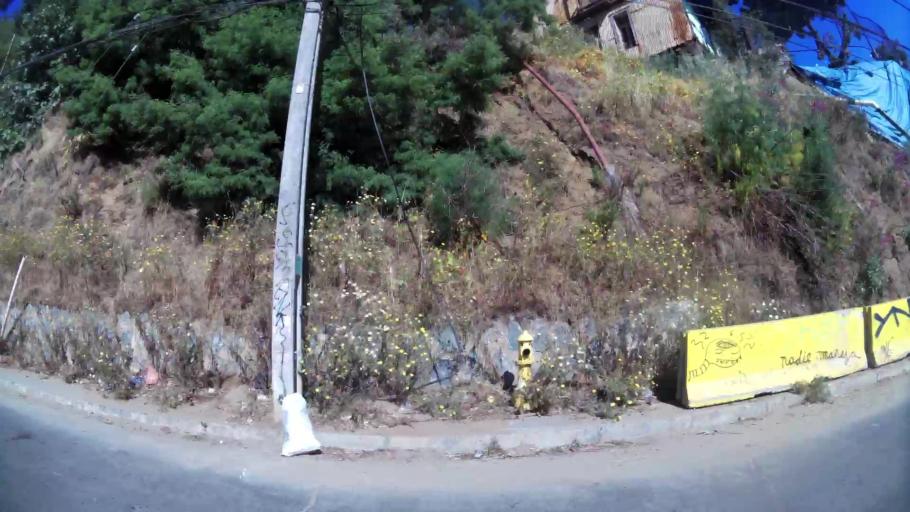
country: CL
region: Valparaiso
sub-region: Provincia de Valparaiso
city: Valparaiso
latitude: -33.0455
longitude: -71.6364
